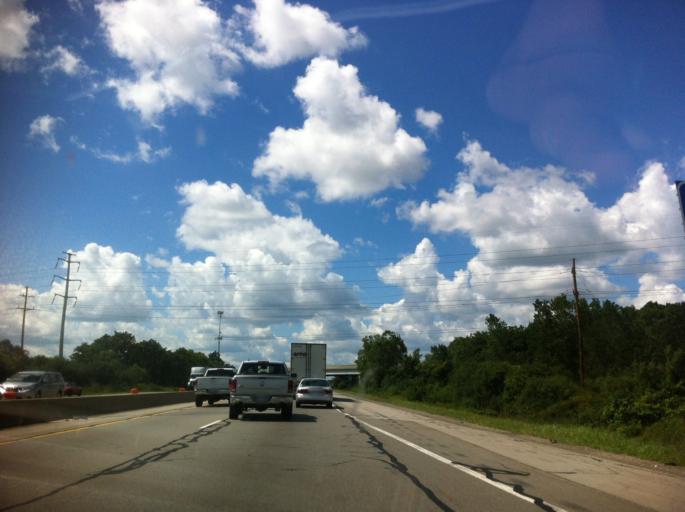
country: US
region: Michigan
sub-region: Washtenaw County
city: Ann Arbor
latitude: 42.2288
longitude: -83.6924
